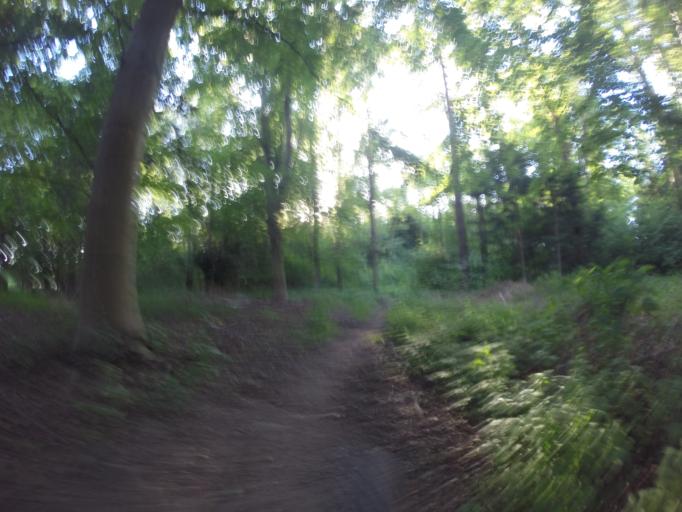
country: DK
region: Capital Region
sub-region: Hoje-Taastrup Kommune
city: Taastrup
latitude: 55.6830
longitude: 12.3125
